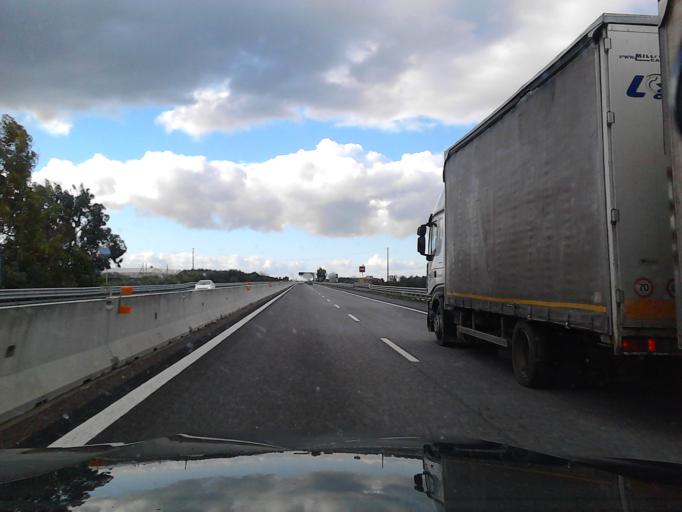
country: IT
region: Apulia
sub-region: Provincia di Barletta - Andria - Trani
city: Andria
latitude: 41.2507
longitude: 16.3205
